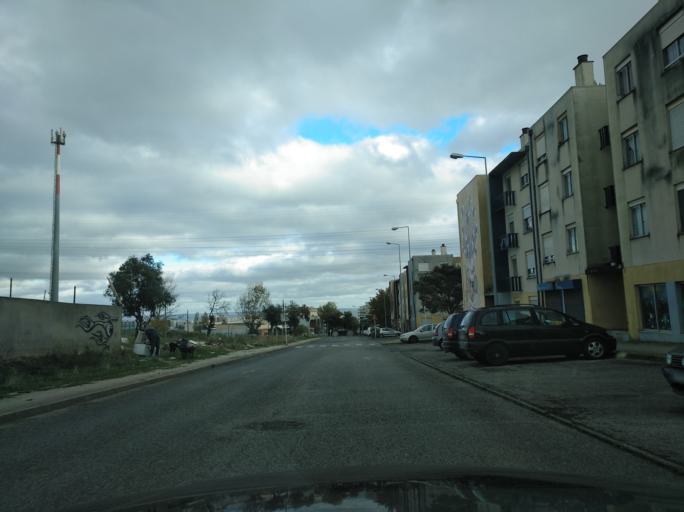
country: PT
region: Lisbon
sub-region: Loures
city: Camarate
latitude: 38.8009
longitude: -9.1169
